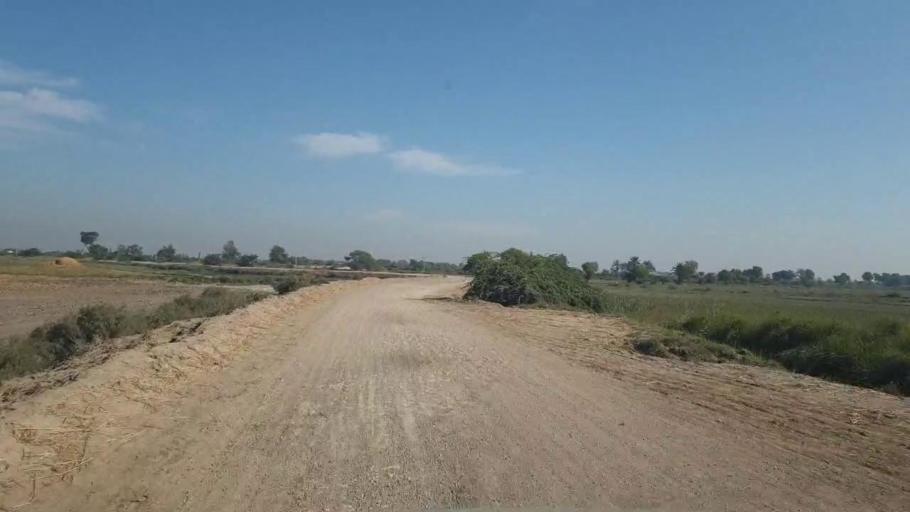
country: PK
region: Sindh
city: Rajo Khanani
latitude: 24.9736
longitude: 68.7767
